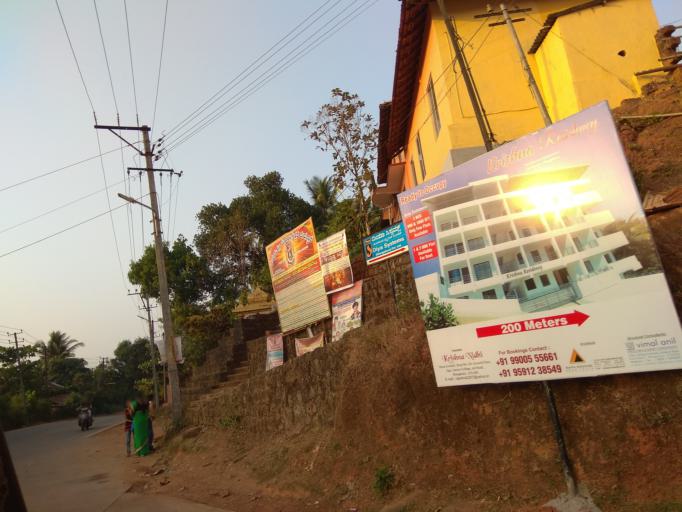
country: IN
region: Karnataka
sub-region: Dakshina Kannada
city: Mangalore
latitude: 12.9181
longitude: 74.8585
